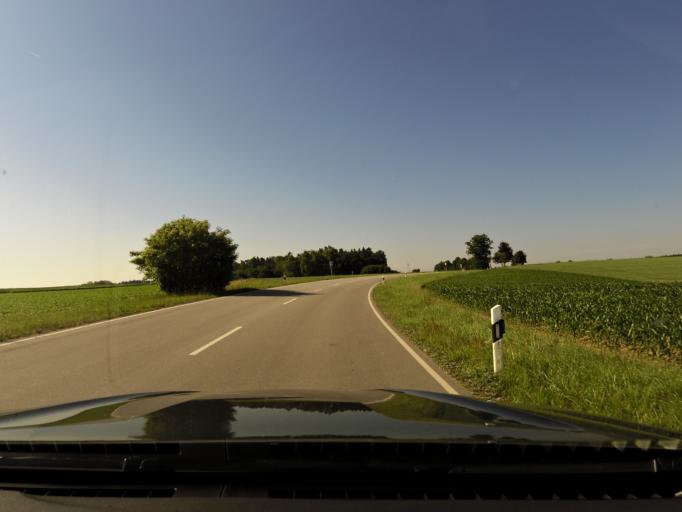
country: DE
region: Bavaria
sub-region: Upper Bavaria
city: Neumarkt-Sankt Veit
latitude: 48.3483
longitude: 12.5104
